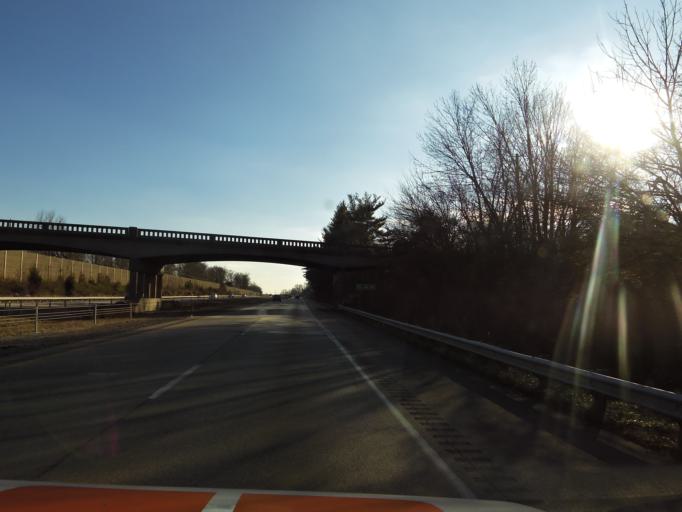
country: US
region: Indiana
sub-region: Clark County
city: Sellersburg
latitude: 38.4104
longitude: -85.7652
